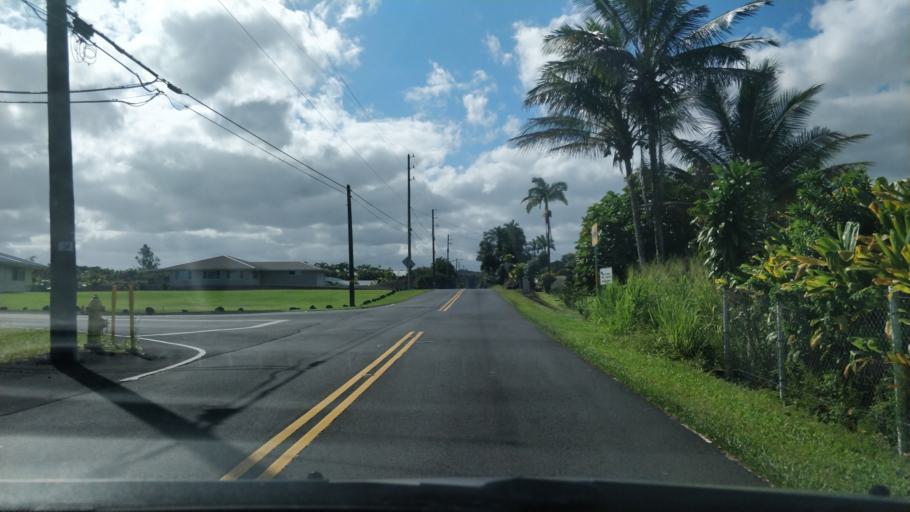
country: US
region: Hawaii
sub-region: Hawaii County
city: Hilo
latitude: 19.6721
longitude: -155.1058
